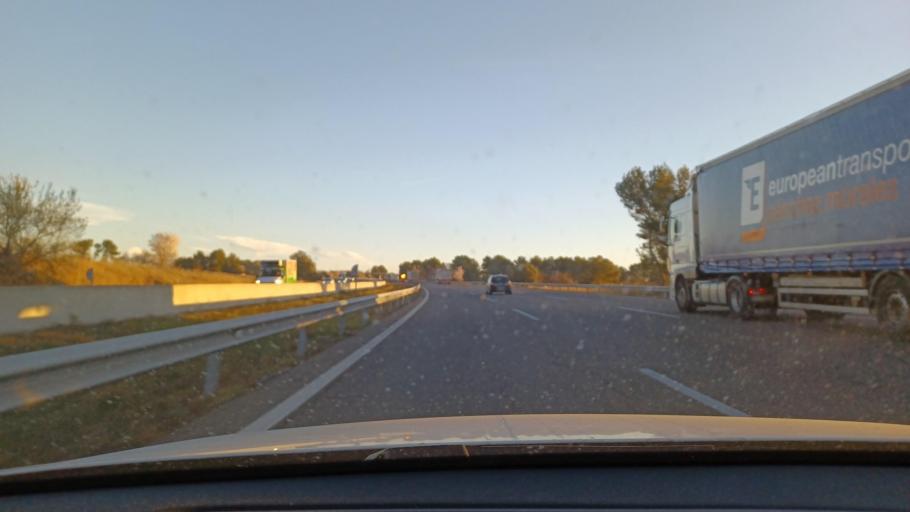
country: ES
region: Catalonia
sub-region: Provincia de Barcelona
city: Castellet
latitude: 41.3172
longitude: 1.6382
